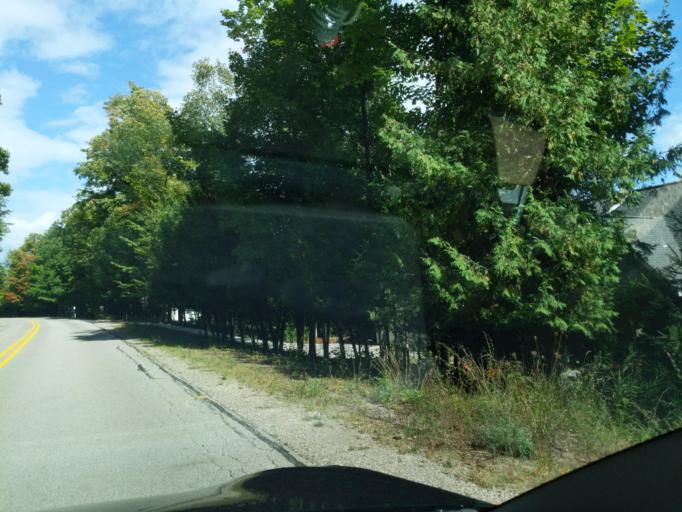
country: US
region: Michigan
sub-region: Antrim County
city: Bellaire
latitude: 44.9647
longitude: -85.3228
